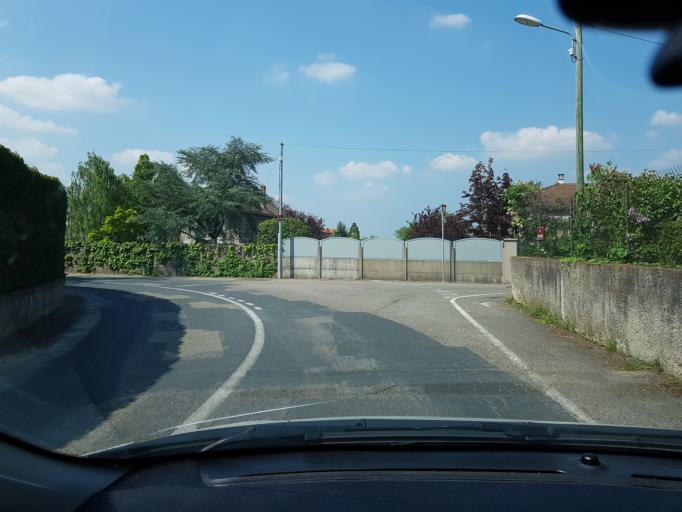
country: FR
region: Rhone-Alpes
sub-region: Departement du Rhone
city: Taluyers
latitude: 45.6386
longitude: 4.7200
